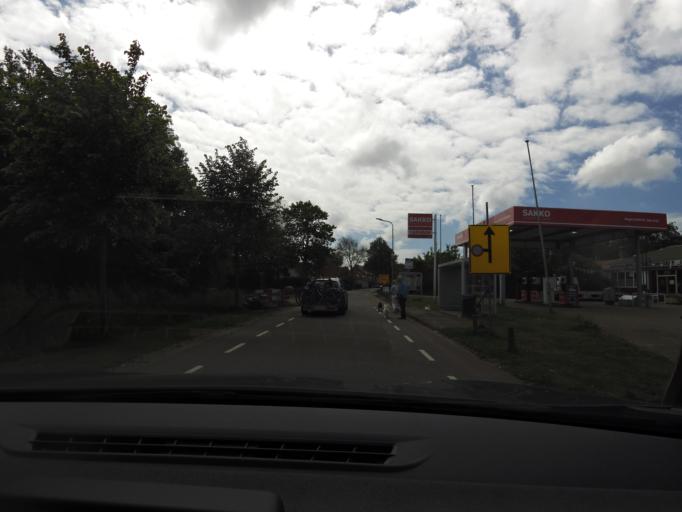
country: NL
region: Zeeland
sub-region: Schouwen-Duiveland
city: Scharendijke
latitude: 51.7304
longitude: 3.8171
